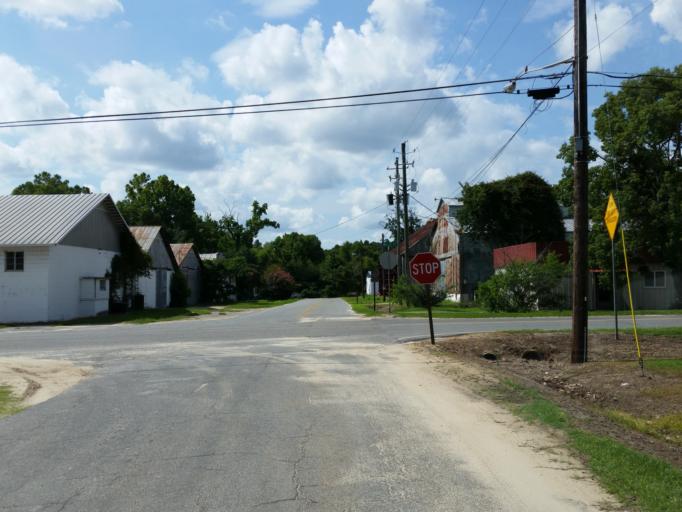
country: US
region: Georgia
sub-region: Turner County
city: Ashburn
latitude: 31.6711
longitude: -83.6347
